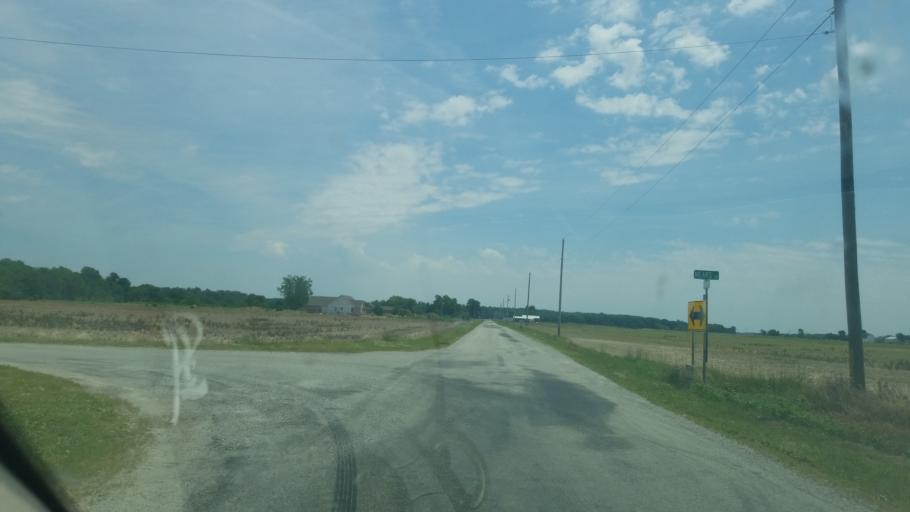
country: US
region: Ohio
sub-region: Wood County
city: North Baltimore
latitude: 41.2219
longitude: -83.6021
